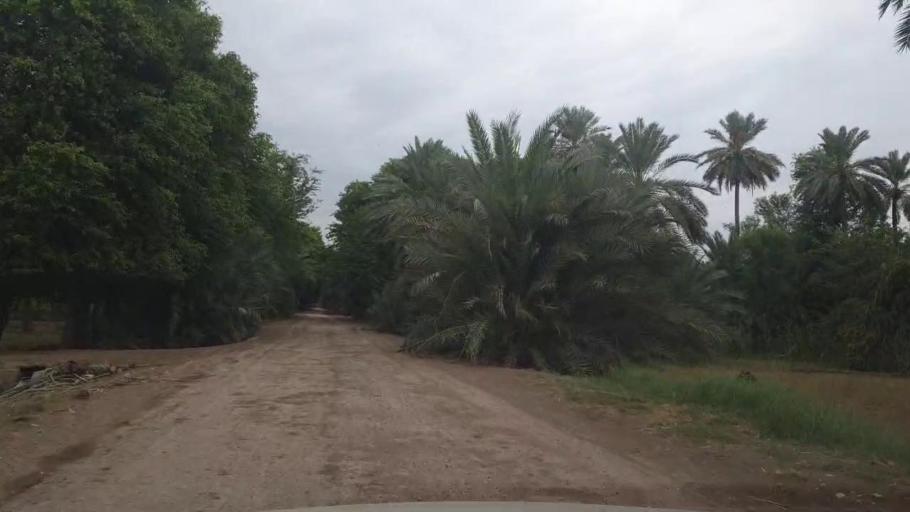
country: PK
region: Sindh
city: Khairpur
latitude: 27.5976
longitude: 68.8147
